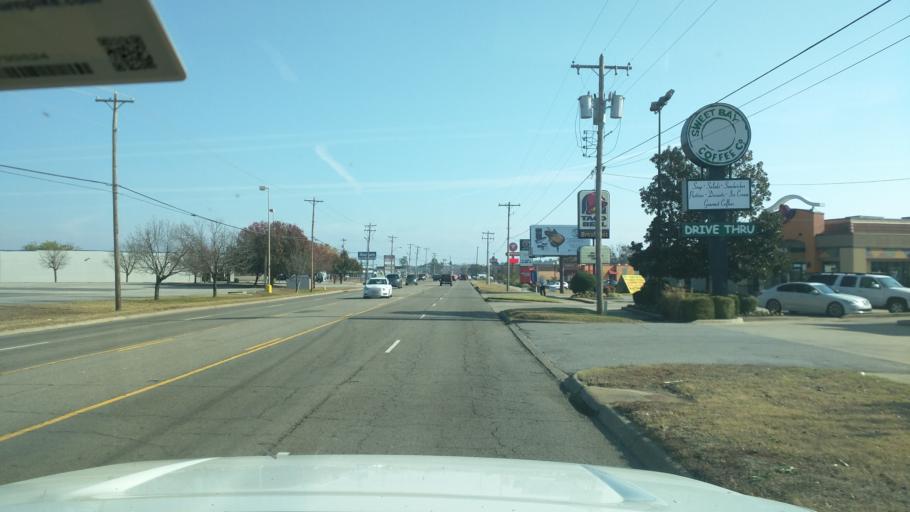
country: US
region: Arkansas
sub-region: Sebastian County
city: Barling
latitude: 35.3497
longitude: -94.3441
